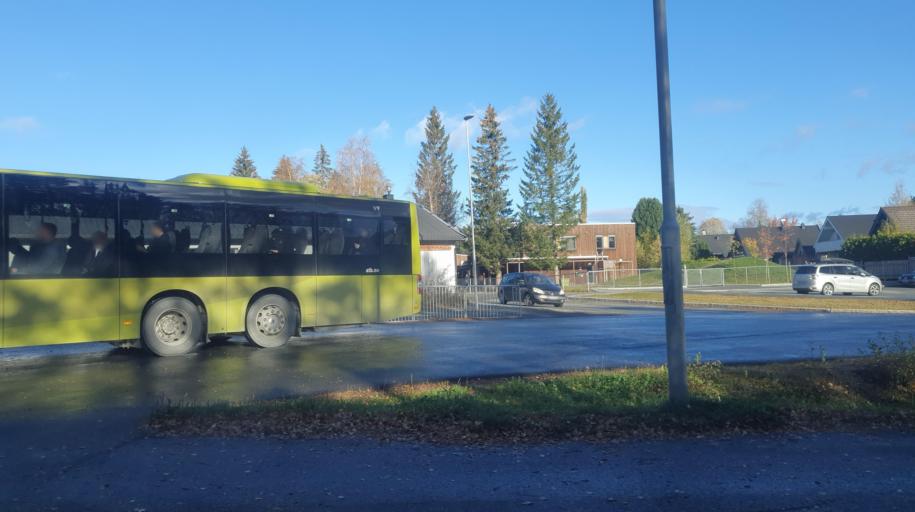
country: NO
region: Sor-Trondelag
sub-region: Klaebu
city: Klaebu
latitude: 63.3067
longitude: 10.4343
